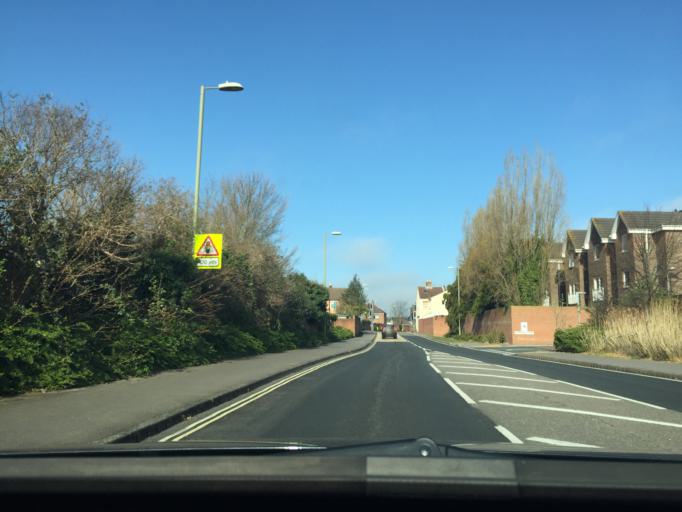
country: GB
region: England
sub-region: Hampshire
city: Gosport
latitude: 50.8106
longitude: -1.1352
